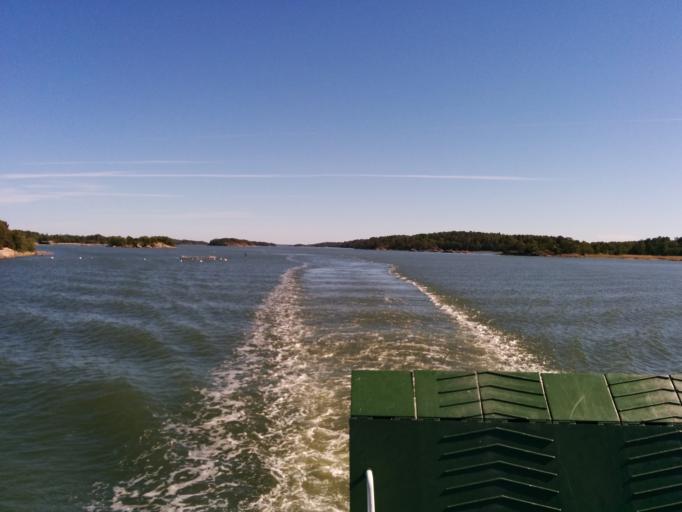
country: FI
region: Varsinais-Suomi
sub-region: Turku
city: Velkua
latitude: 60.4581
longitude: 21.7002
